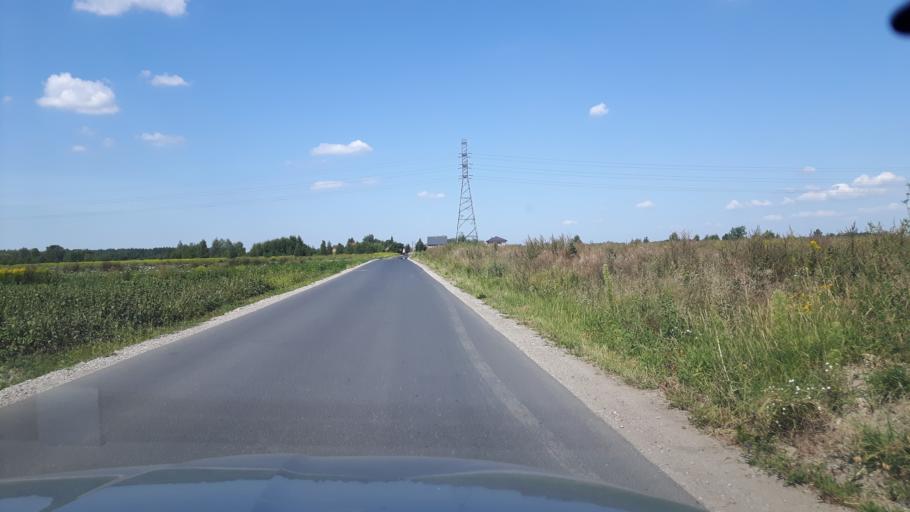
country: PL
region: Masovian Voivodeship
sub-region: Powiat pruszkowski
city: Michalowice
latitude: 52.1325
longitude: 20.8608
